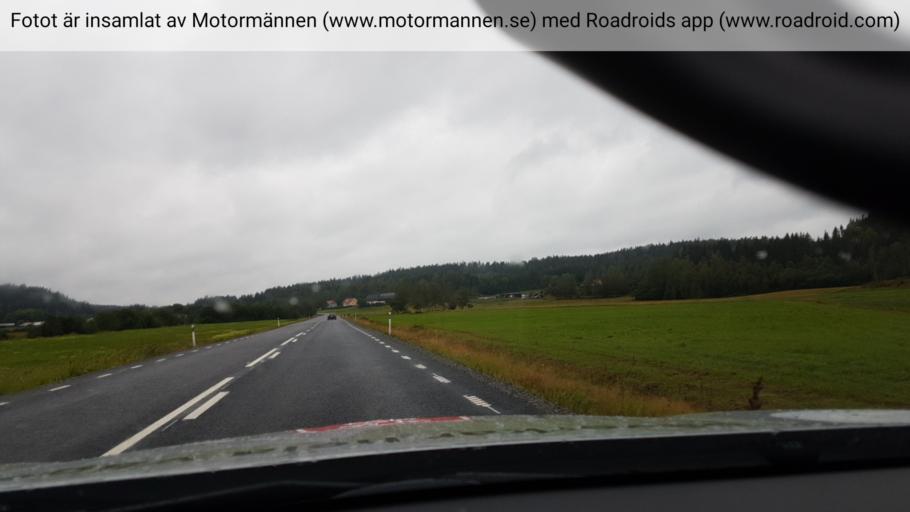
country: SE
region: Vaestra Goetaland
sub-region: Dals-Ed Kommun
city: Ed
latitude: 58.9145
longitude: 12.0176
